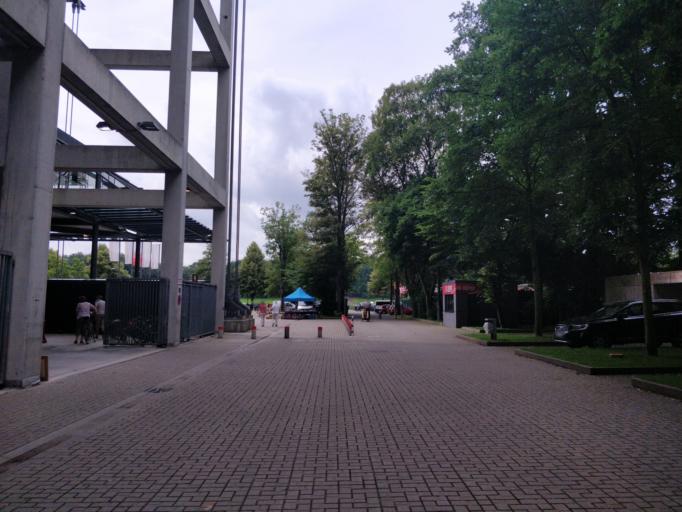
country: DE
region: North Rhine-Westphalia
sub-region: Regierungsbezirk Koln
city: Mengenich
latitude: 50.9331
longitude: 6.8737
